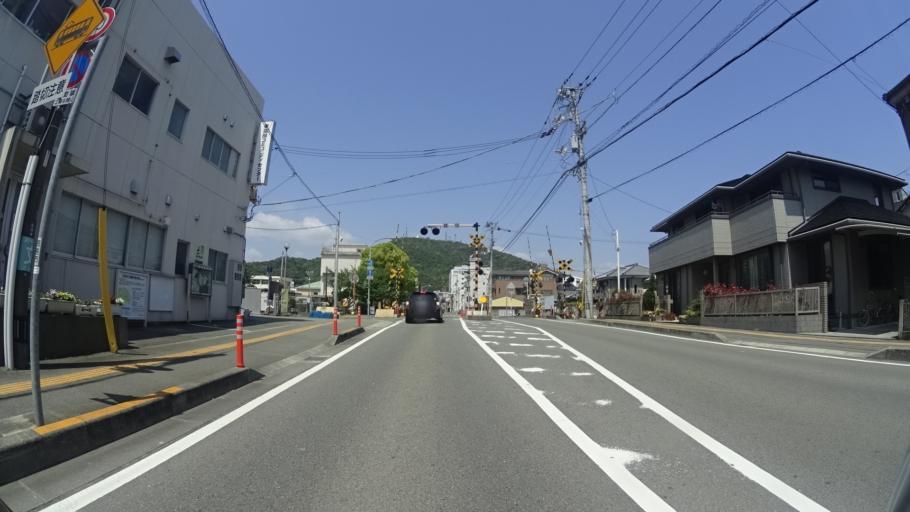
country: JP
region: Tokushima
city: Tokushima-shi
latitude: 34.0621
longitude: 134.5550
